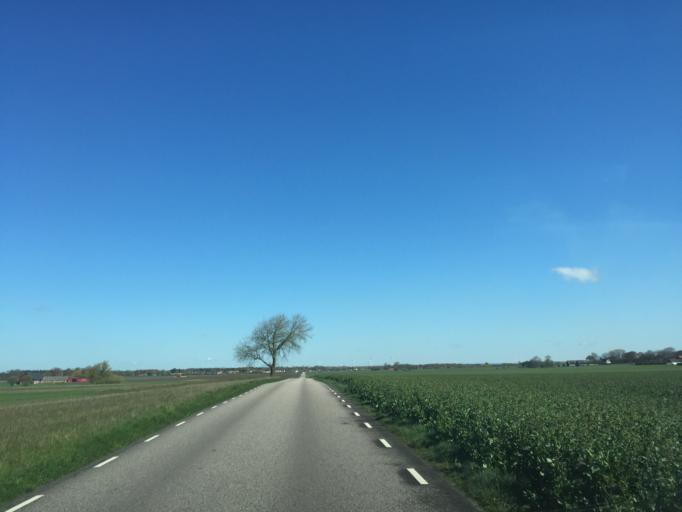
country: SE
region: Skane
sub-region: Kavlinge Kommun
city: Loddekopinge
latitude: 55.8020
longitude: 13.0250
